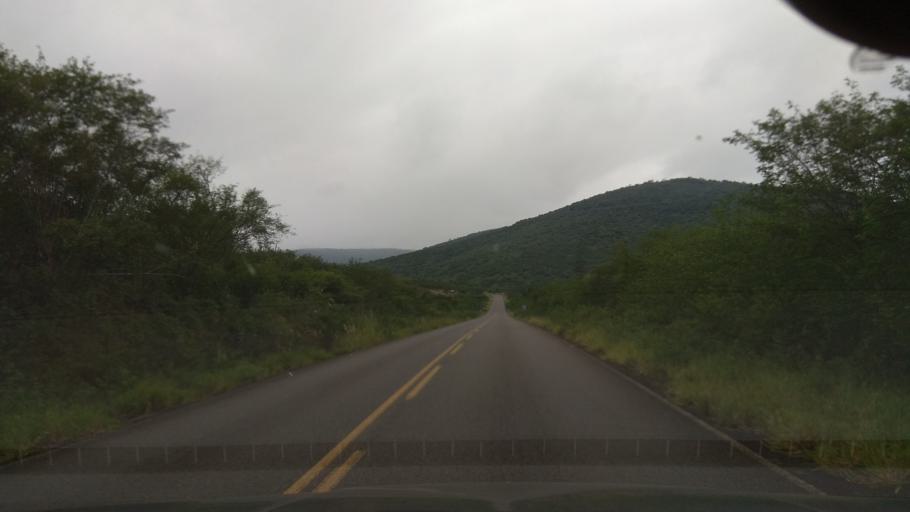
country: BR
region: Bahia
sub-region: Santa Ines
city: Santa Ines
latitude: -13.2515
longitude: -39.7725
